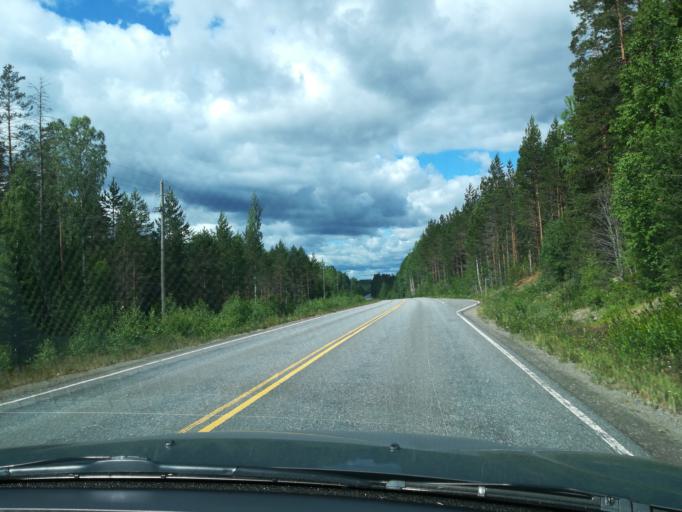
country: FI
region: Southern Savonia
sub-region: Mikkeli
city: Maentyharju
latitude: 61.3648
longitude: 26.9839
